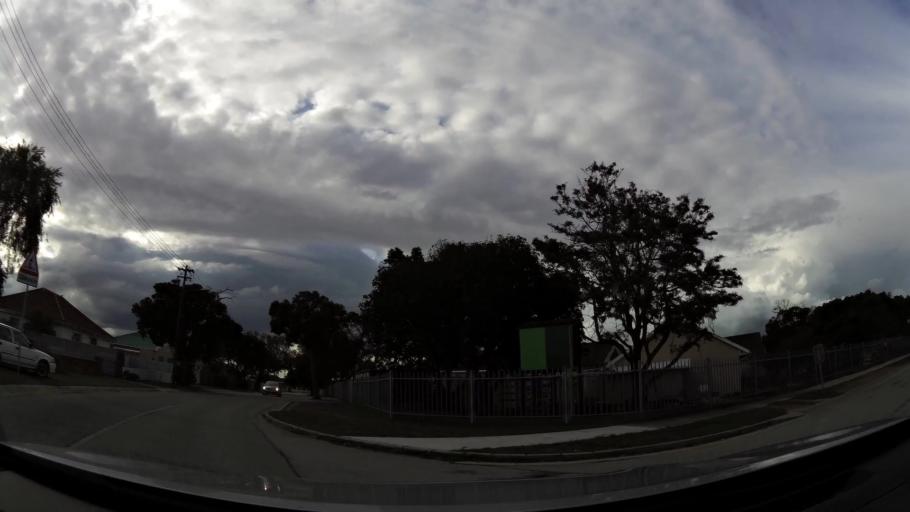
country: ZA
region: Eastern Cape
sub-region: Nelson Mandela Bay Metropolitan Municipality
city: Port Elizabeth
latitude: -33.9421
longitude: 25.5129
